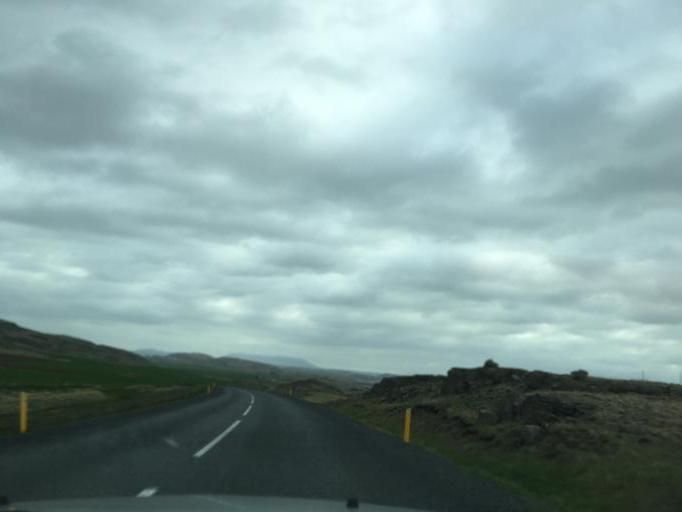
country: IS
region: South
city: Vestmannaeyjar
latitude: 64.2344
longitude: -20.2382
